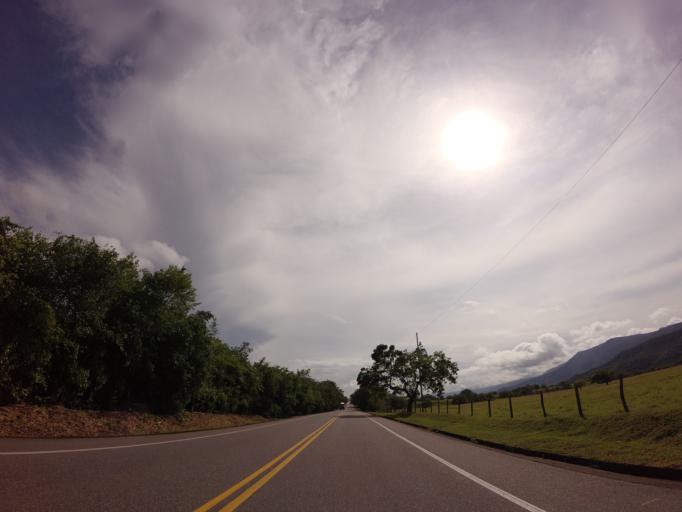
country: CO
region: Tolima
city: Honda
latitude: 5.2985
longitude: -74.7439
